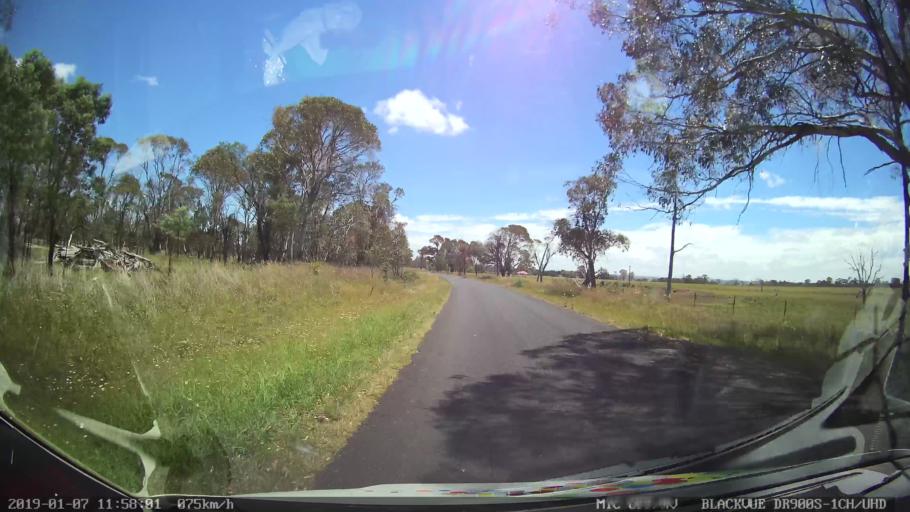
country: AU
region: New South Wales
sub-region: Guyra
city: Guyra
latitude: -30.2579
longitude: 151.6669
